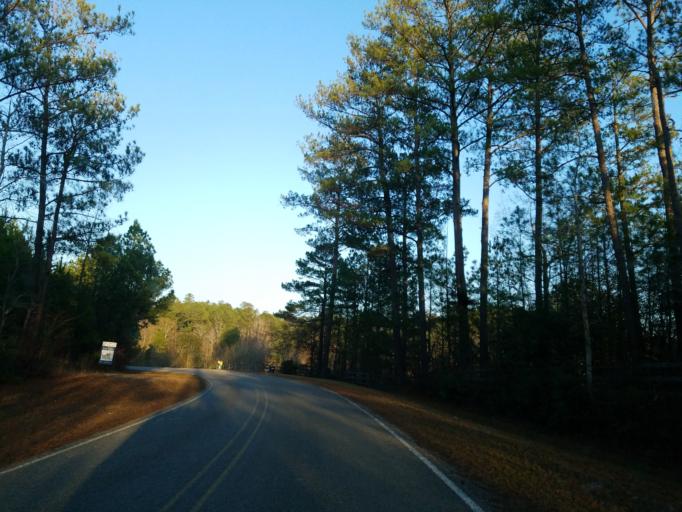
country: US
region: Mississippi
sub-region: Lauderdale County
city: Meridian
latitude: 32.2649
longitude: -88.7811
